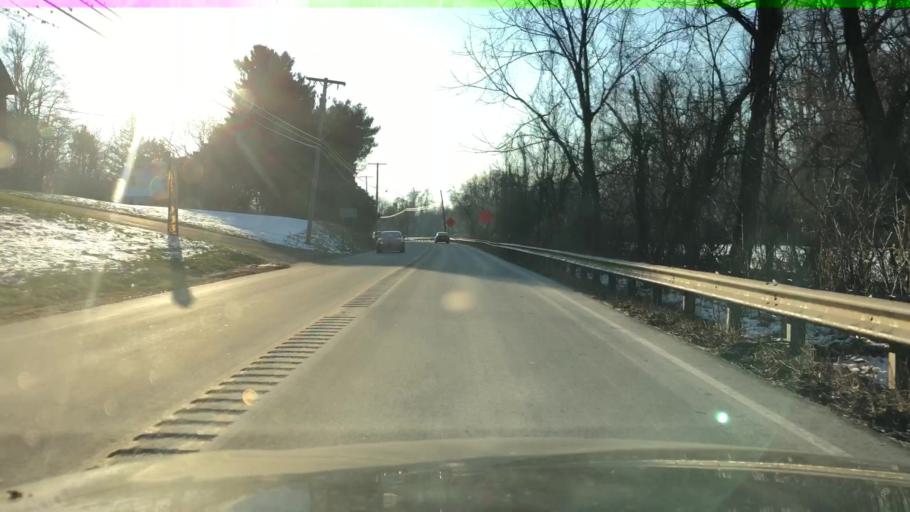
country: US
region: New Jersey
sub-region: Hunterdon County
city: Lambertville
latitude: 40.3434
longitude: -74.9411
